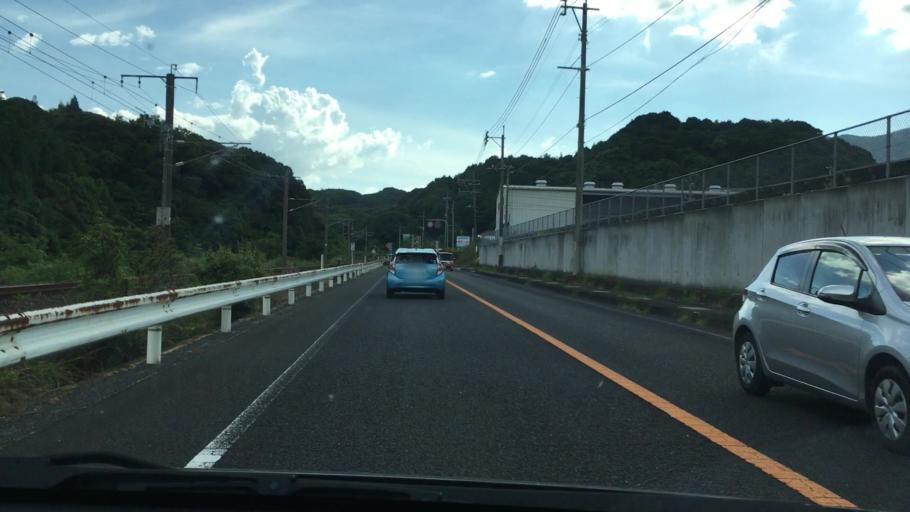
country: JP
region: Saga Prefecture
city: Imaricho-ko
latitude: 33.1754
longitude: 129.8487
